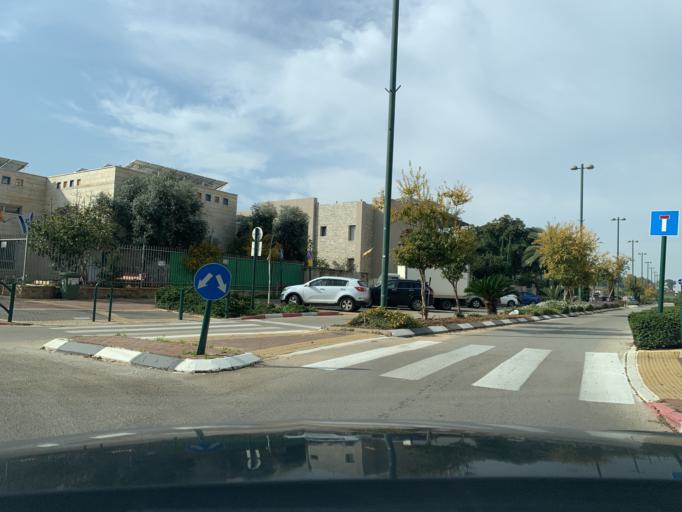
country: IL
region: Central District
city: Kfar Saba
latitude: 32.1851
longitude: 34.9280
